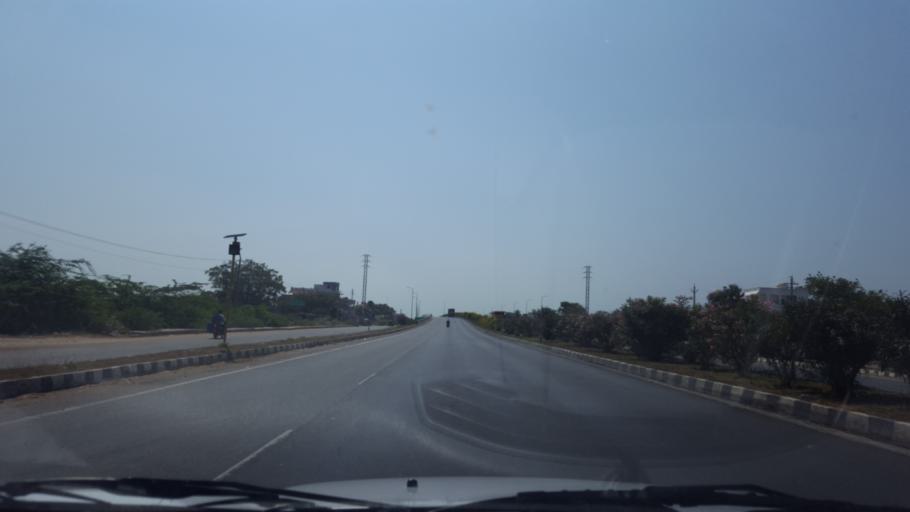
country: IN
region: Andhra Pradesh
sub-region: Prakasam
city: Addanki
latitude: 15.6621
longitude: 80.0153
